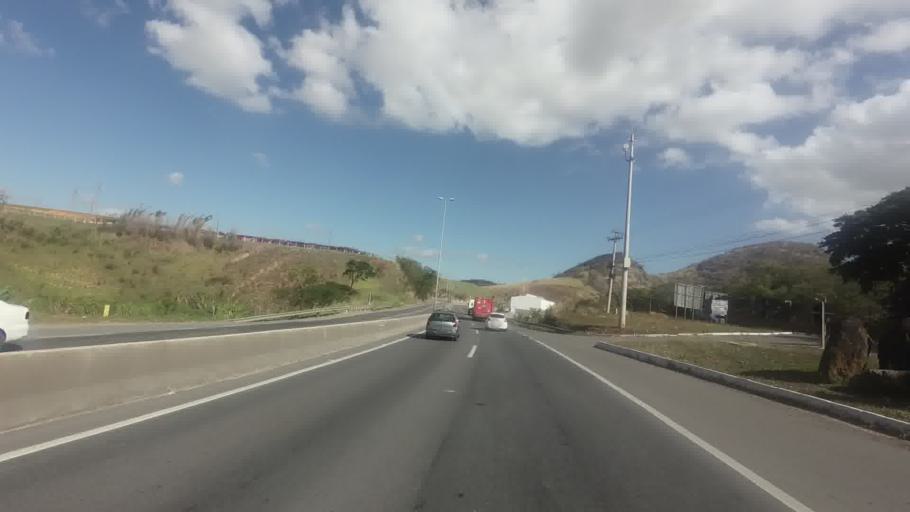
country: BR
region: Espirito Santo
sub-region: Viana
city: Viana
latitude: -20.3704
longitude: -40.4439
